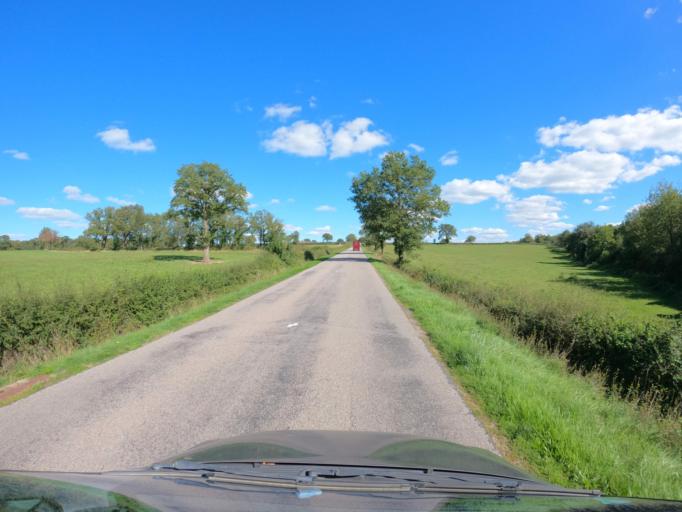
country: FR
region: Auvergne
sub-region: Departement de l'Allier
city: Doyet
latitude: 46.3976
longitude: 2.8754
